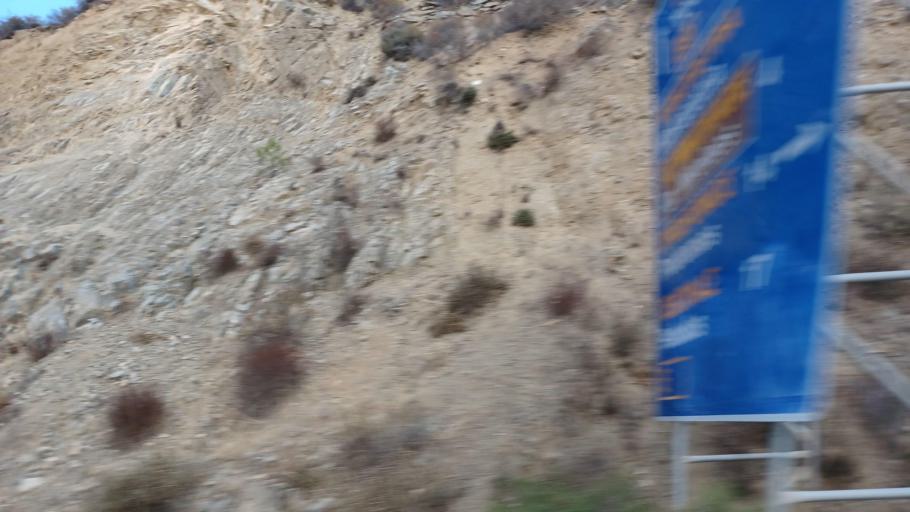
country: CY
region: Lefkosia
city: Kakopetria
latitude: 34.9794
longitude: 32.9086
